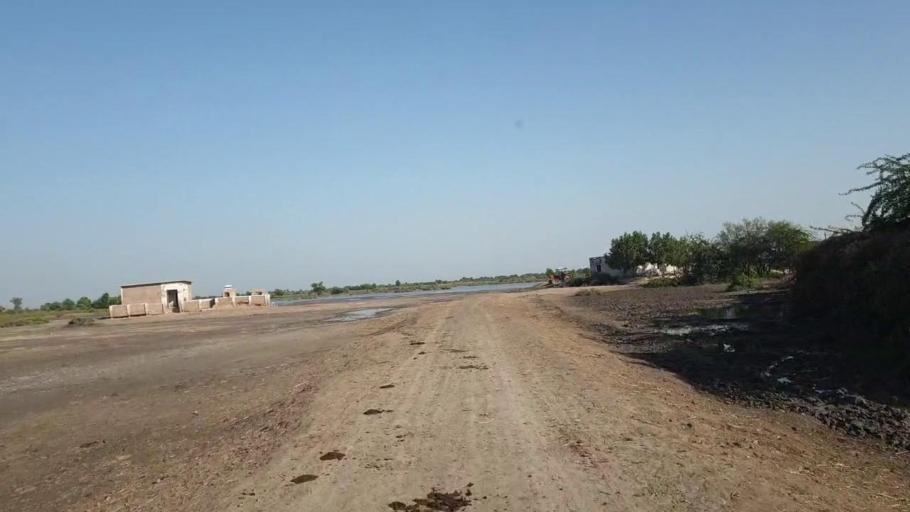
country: PK
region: Sindh
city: Badin
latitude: 24.5919
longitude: 68.9122
